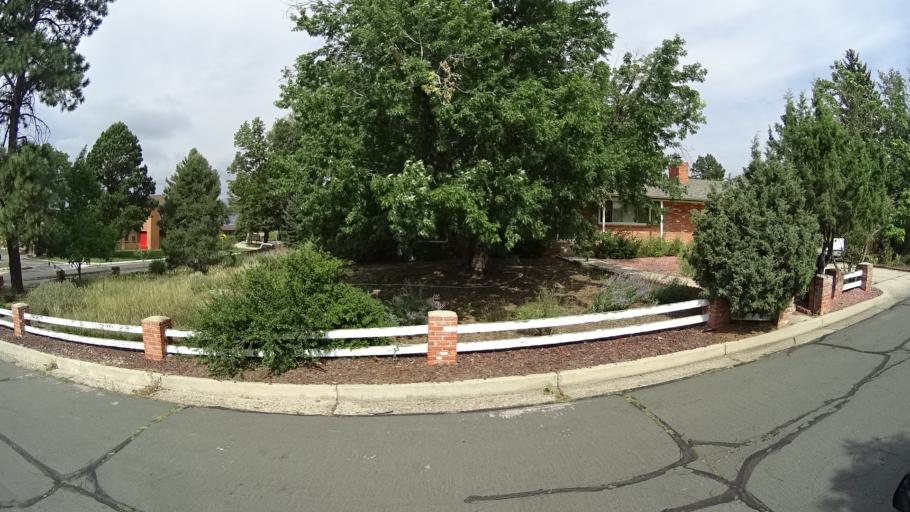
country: US
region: Colorado
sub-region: El Paso County
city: Colorado Springs
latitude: 38.8888
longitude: -104.8012
